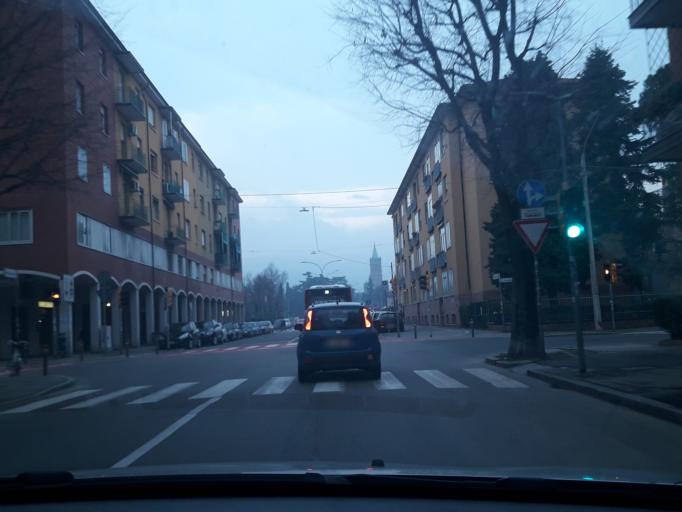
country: IT
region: Emilia-Romagna
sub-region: Provincia di Bologna
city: Bologna
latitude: 44.5010
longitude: 11.3112
